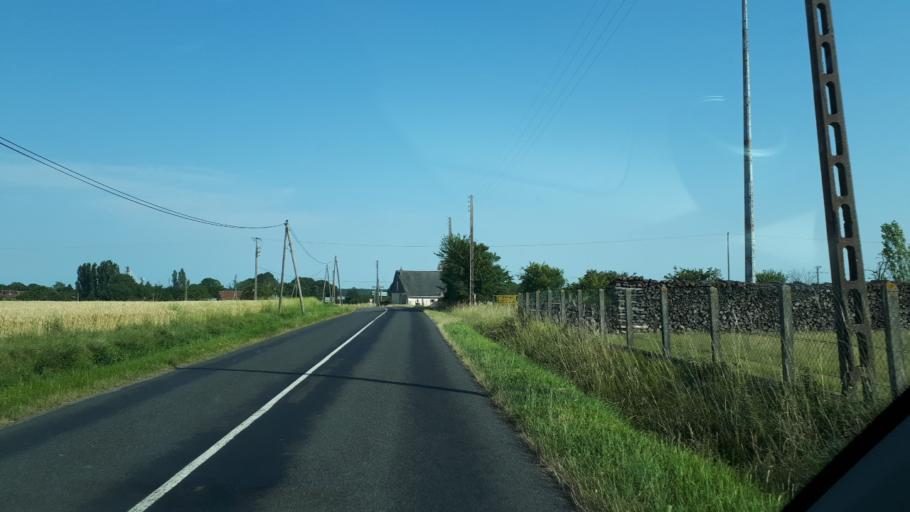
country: FR
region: Centre
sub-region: Departement du Loir-et-Cher
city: La Ville-aux-Clercs
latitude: 47.9594
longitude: 1.0726
